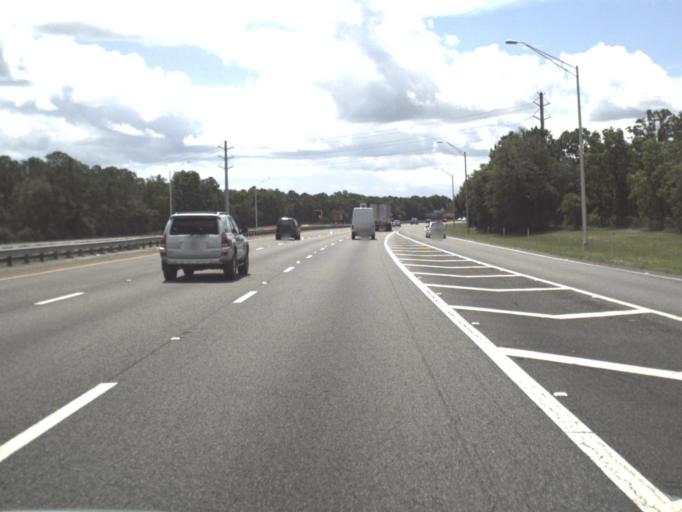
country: US
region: Florida
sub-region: Flagler County
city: Palm Coast
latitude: 29.6606
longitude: -81.2845
